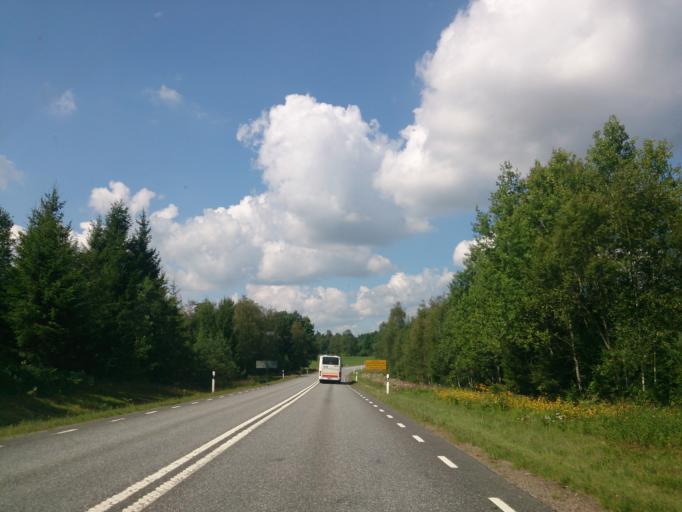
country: SE
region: Joenkoeping
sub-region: Gislaveds Kommun
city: Reftele
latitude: 57.1759
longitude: 13.6391
